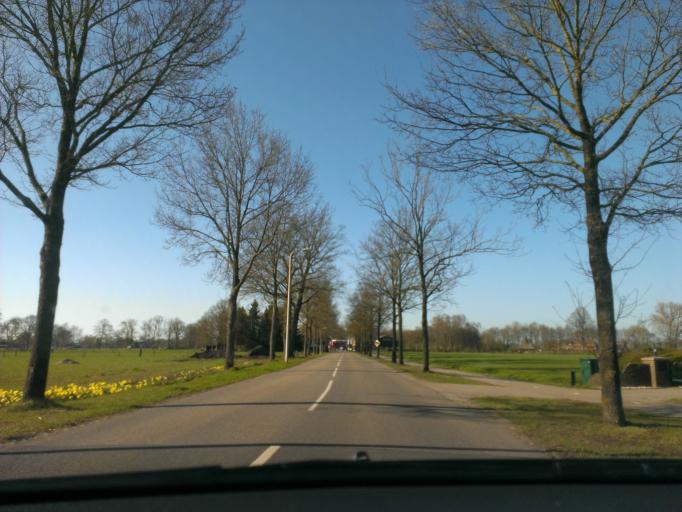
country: NL
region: Overijssel
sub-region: Gemeente Twenterand
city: Den Ham
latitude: 52.4202
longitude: 6.4832
